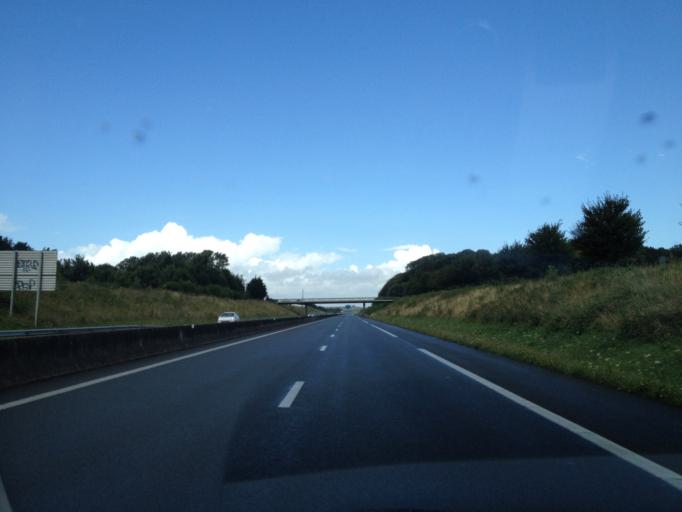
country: FR
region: Nord-Pas-de-Calais
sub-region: Departement du Pas-de-Calais
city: Verton
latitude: 50.3993
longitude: 1.6943
